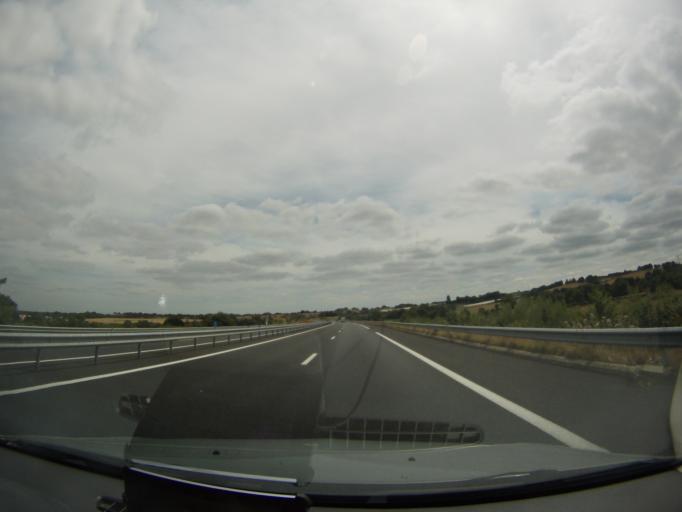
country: FR
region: Pays de la Loire
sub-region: Departement de Maine-et-Loire
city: La Tessoualle
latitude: 46.9998
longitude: -0.8627
